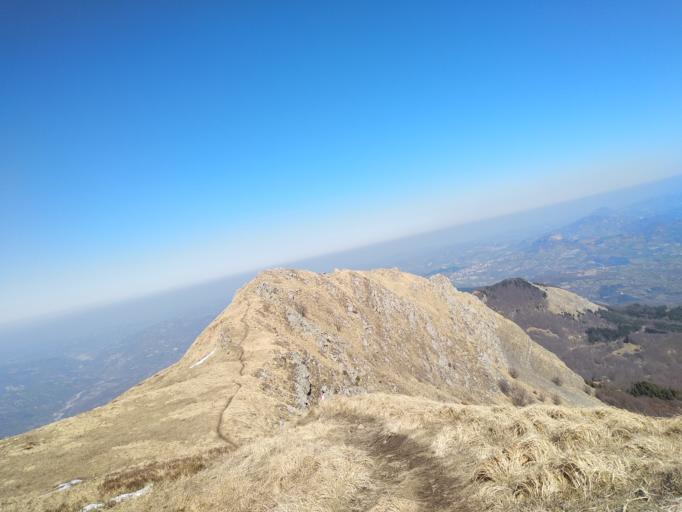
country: IT
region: Emilia-Romagna
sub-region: Provincia di Reggio Emilia
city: Collagna
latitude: 44.3770
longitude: 10.2891
